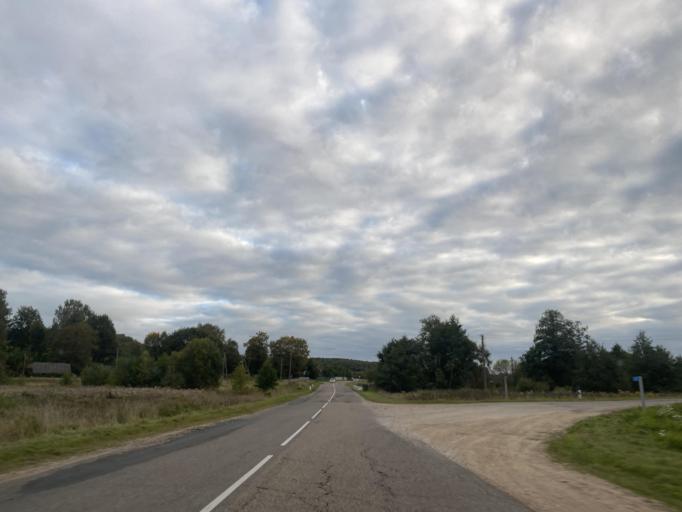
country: BY
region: Grodnenskaya
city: Kreva
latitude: 54.3056
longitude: 26.2788
